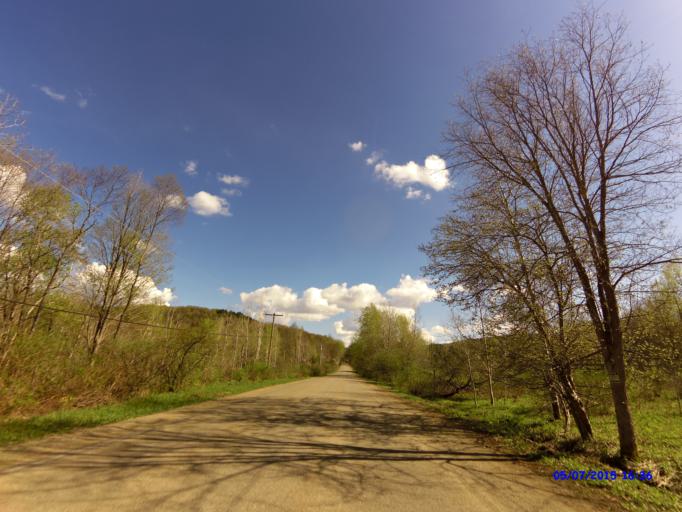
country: US
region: New York
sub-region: Cattaraugus County
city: Little Valley
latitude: 42.3246
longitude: -78.6919
